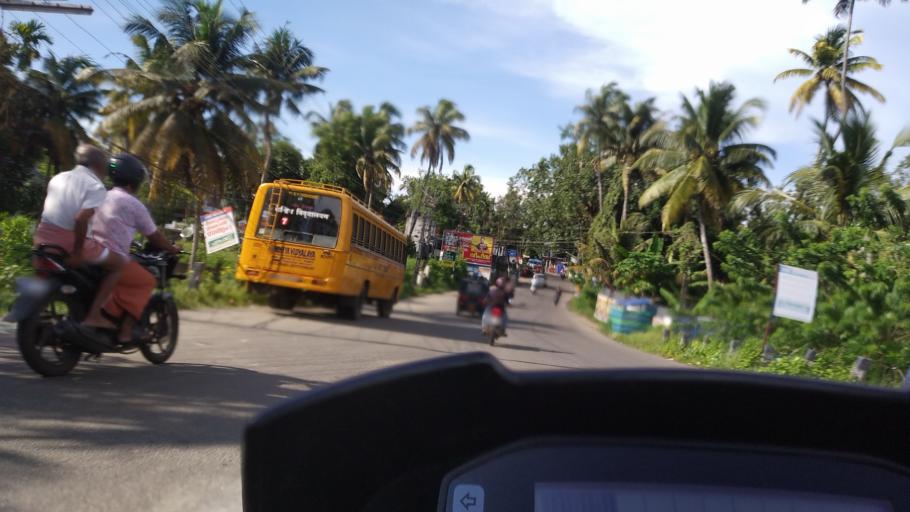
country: IN
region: Kerala
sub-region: Ernakulam
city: Elur
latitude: 10.0549
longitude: 76.2155
